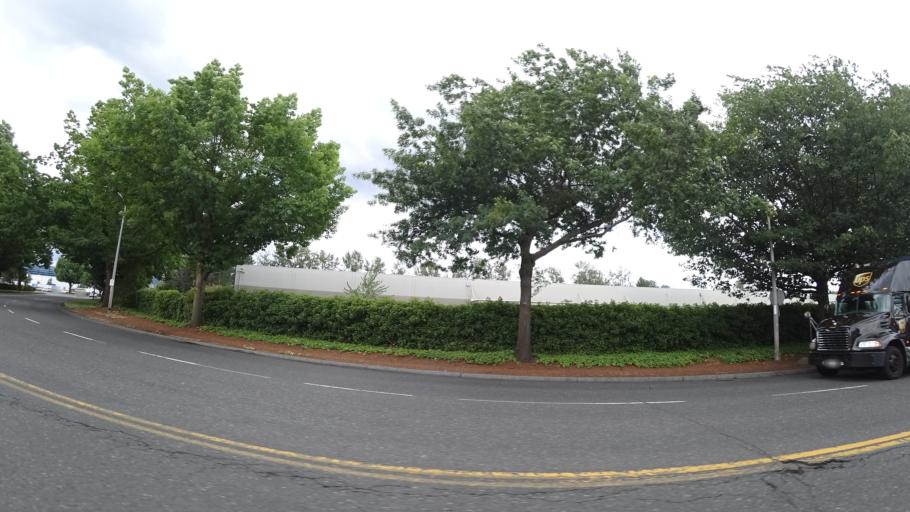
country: US
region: Oregon
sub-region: Multnomah County
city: Portland
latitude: 45.5643
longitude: -122.7057
